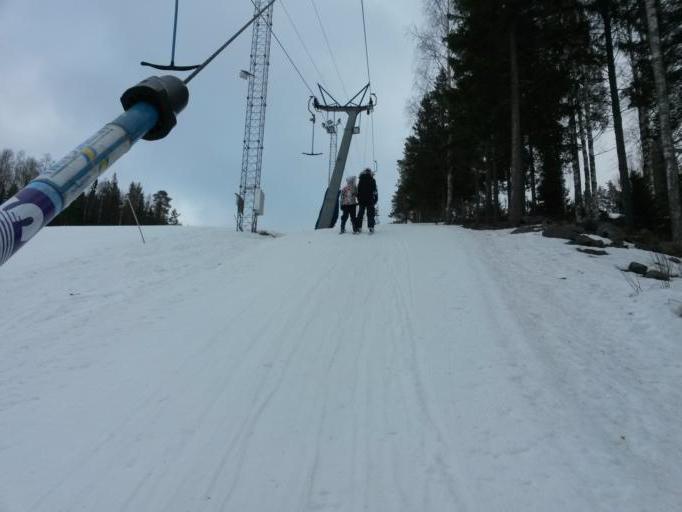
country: SE
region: Vaesterbotten
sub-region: Skelleftea Kommun
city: Viken
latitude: 64.7212
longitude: 20.7843
